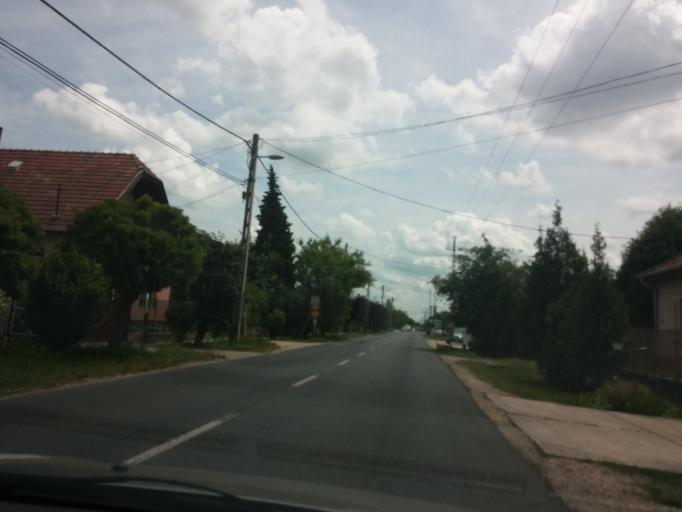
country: HU
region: Pest
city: Toekoel
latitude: 47.3100
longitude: 18.9689
